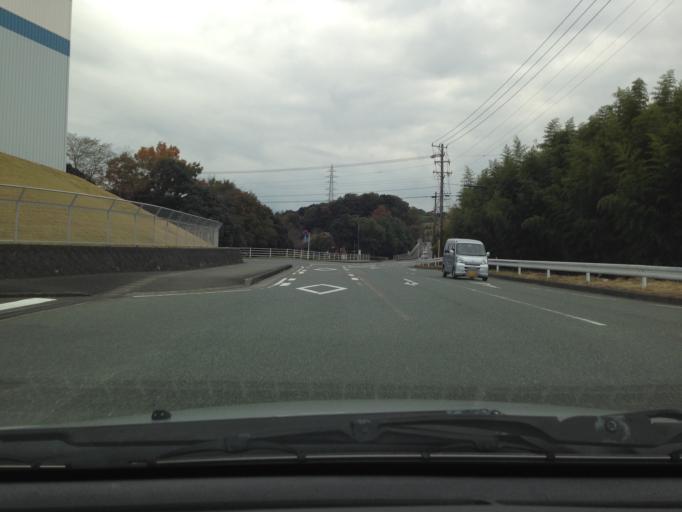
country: JP
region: Shizuoka
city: Fukuroi
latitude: 34.7468
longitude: 137.9454
